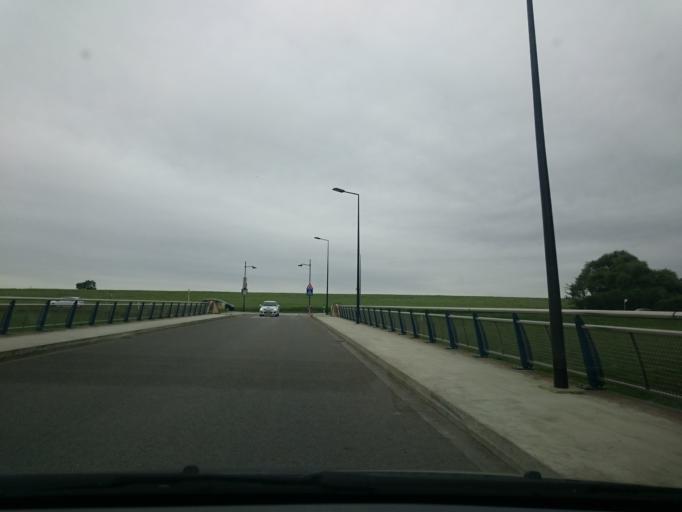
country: LU
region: Luxembourg
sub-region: Canton de Luxembourg
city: Luxembourg
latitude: 49.5897
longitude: 6.0991
